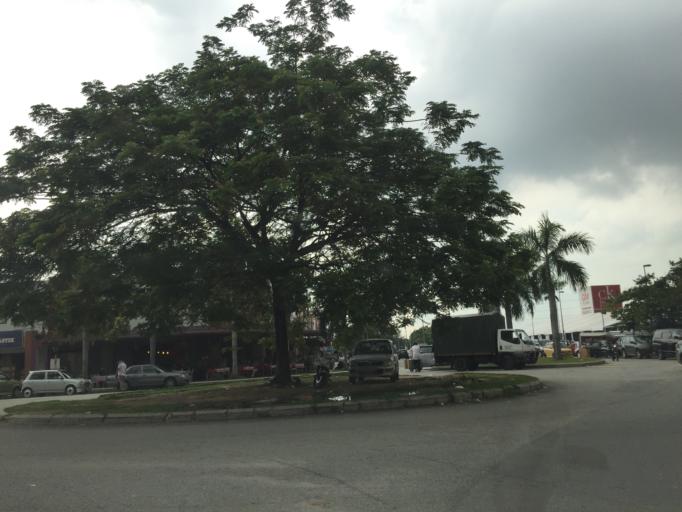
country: MY
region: Selangor
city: Klang
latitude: 2.9907
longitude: 101.4508
